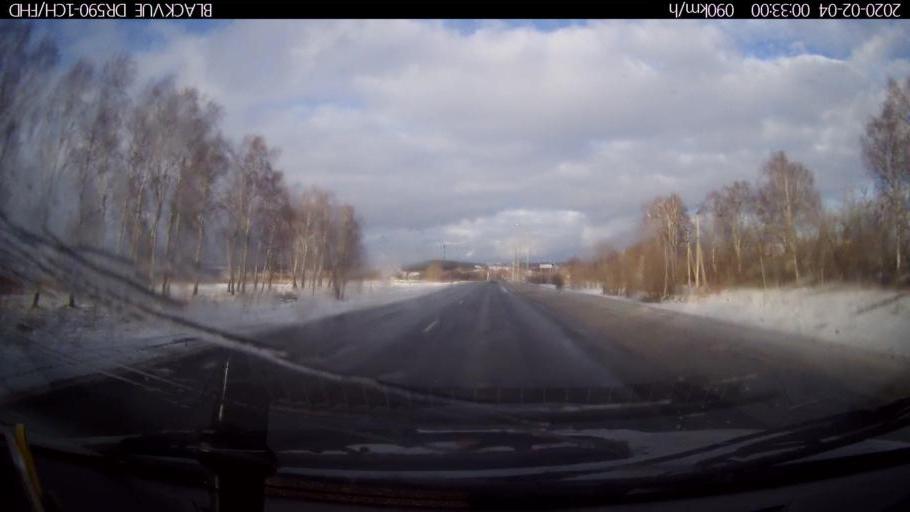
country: RU
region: Nizjnij Novgorod
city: Kstovo
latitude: 56.0665
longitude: 44.1399
